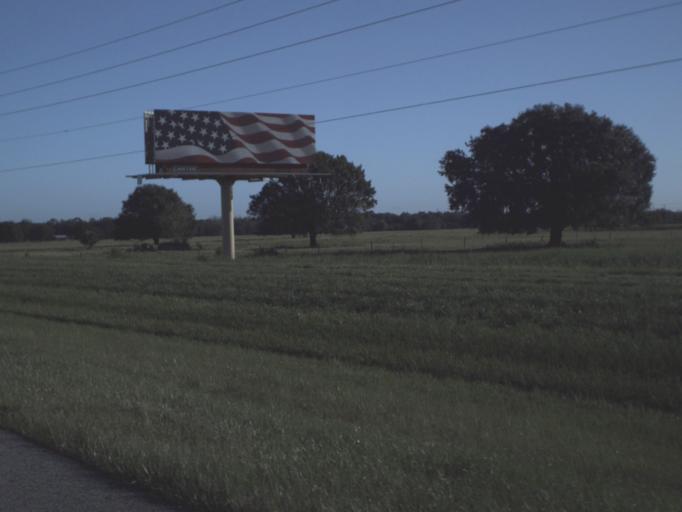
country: US
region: Florida
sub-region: Charlotte County
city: Harbour Heights
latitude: 27.0567
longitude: -81.9582
